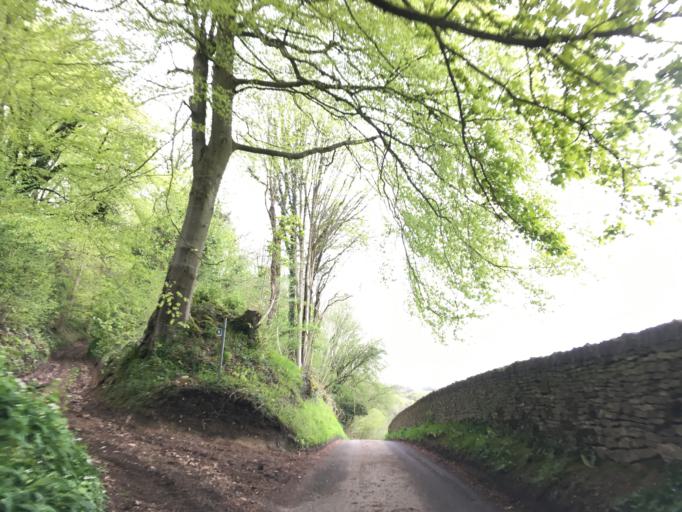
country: GB
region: England
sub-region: Gloucestershire
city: Wotton-under-Edge
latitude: 51.6334
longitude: -2.3005
